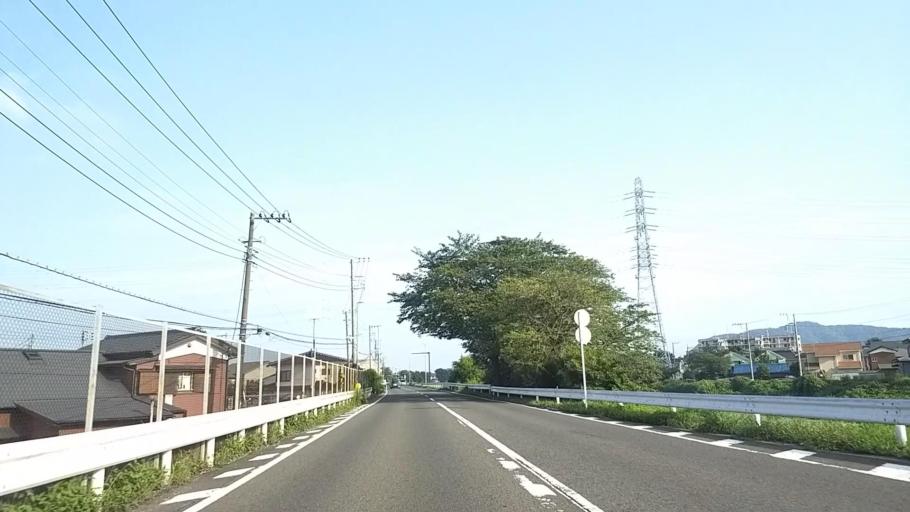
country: JP
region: Kanagawa
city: Hiratsuka
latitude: 35.3478
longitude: 139.3166
